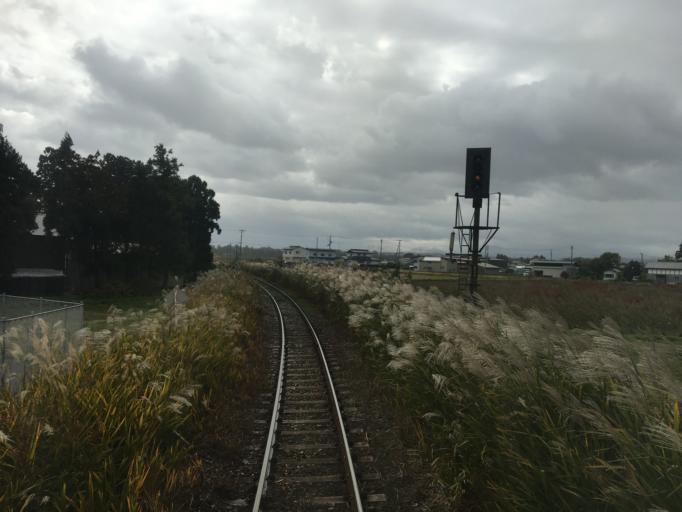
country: JP
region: Yamagata
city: Nagai
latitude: 38.0735
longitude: 140.0289
